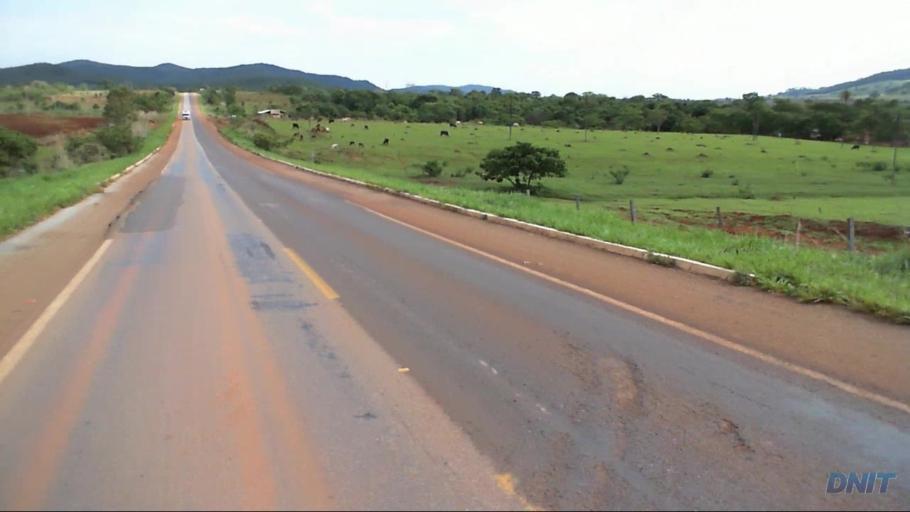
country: BR
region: Goias
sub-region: Barro Alto
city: Barro Alto
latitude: -14.9590
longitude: -48.9317
